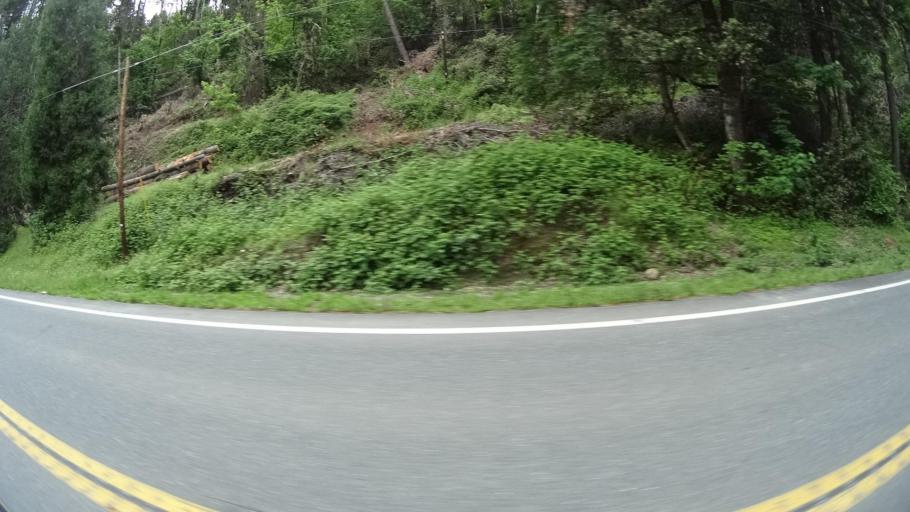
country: US
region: California
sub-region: Humboldt County
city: Willow Creek
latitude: 40.9849
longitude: -123.6394
